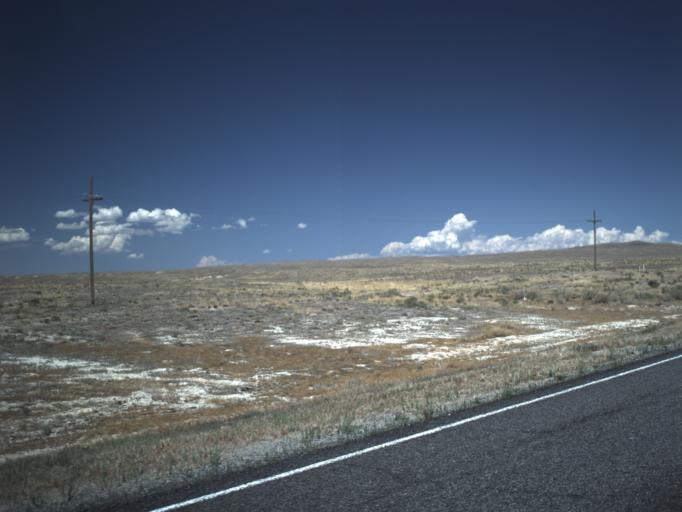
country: US
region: Utah
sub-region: Millard County
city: Delta
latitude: 39.1250
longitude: -113.1124
